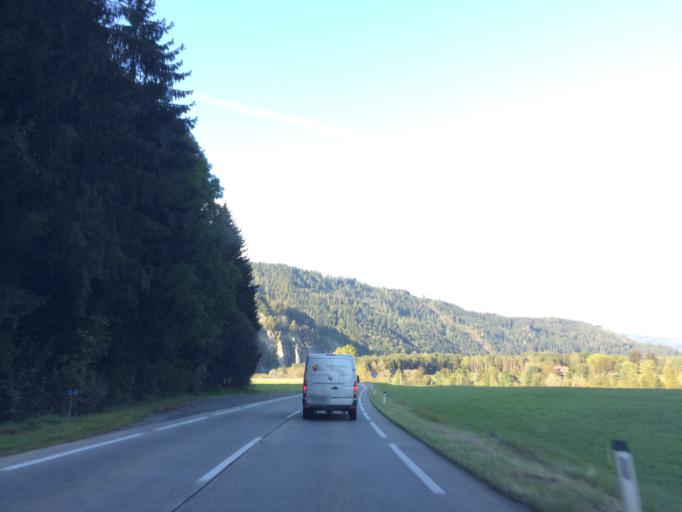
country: AT
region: Styria
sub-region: Politischer Bezirk Leoben
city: Leoben
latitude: 47.3458
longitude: 15.0511
